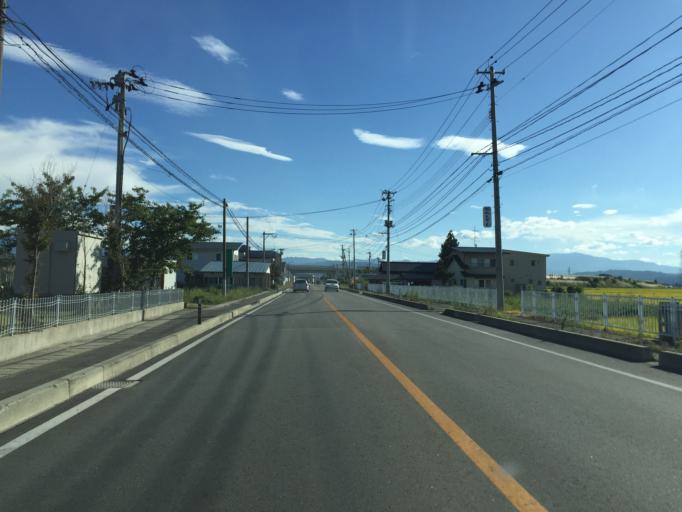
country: JP
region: Yamagata
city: Takahata
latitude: 37.9738
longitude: 140.1331
